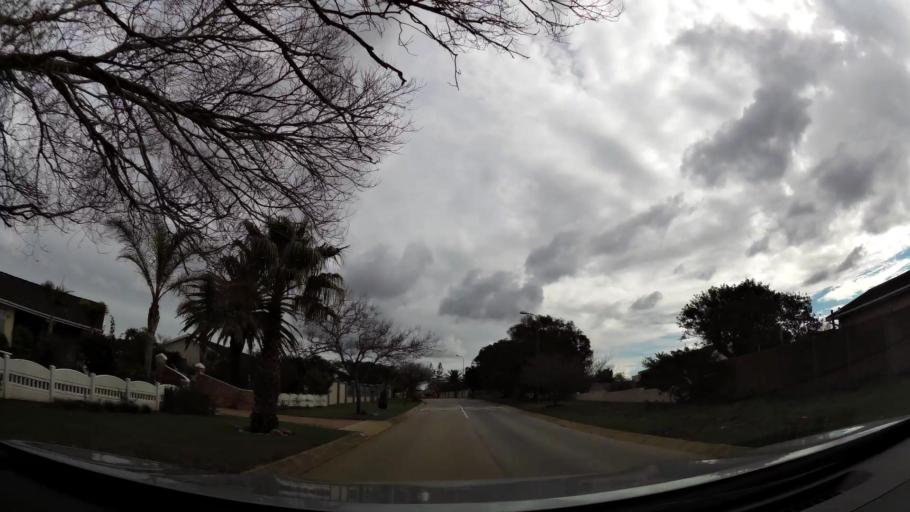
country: ZA
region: Eastern Cape
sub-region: Nelson Mandela Bay Metropolitan Municipality
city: Port Elizabeth
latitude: -33.9315
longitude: 25.5261
